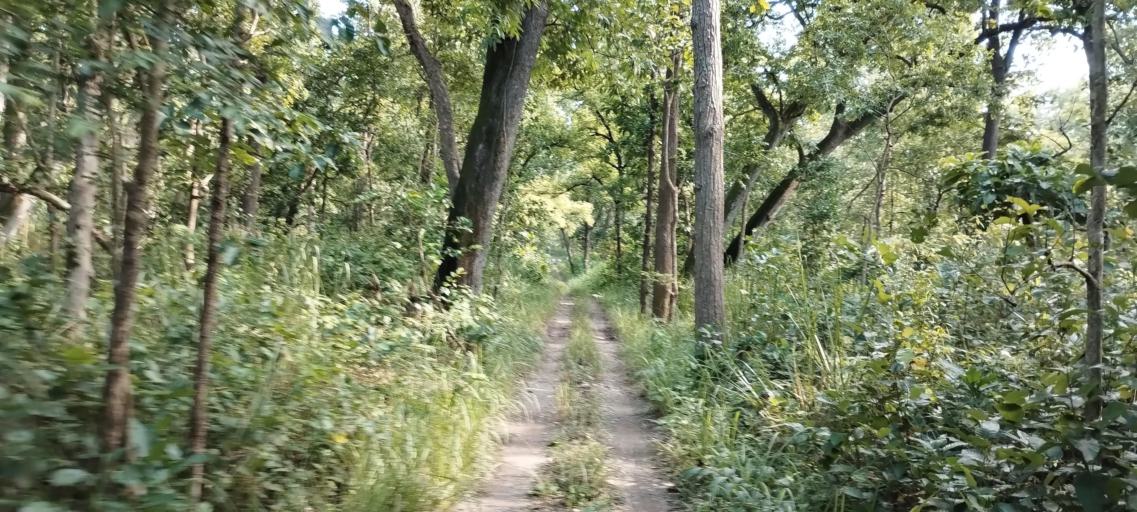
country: NP
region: Far Western
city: Tikapur
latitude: 28.5445
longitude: 81.2865
